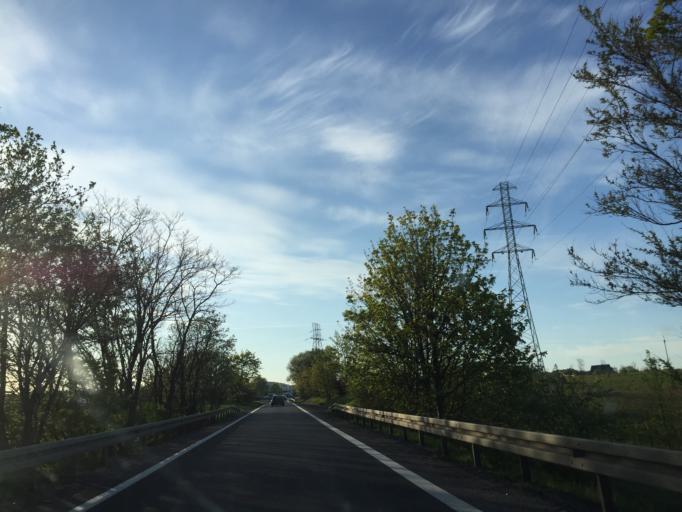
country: PL
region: Pomeranian Voivodeship
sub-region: Powiat gdanski
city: Kowale
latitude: 54.3254
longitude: 18.5432
